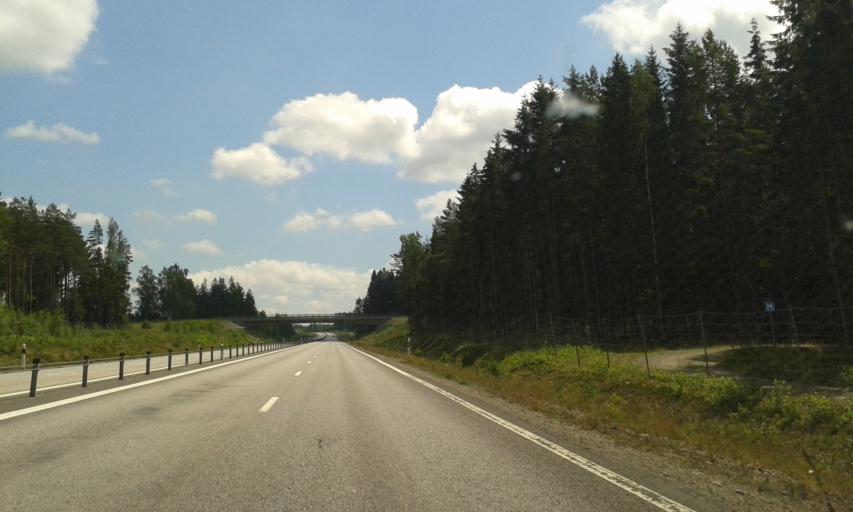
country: SE
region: Kronoberg
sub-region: Vaxjo Kommun
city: Gemla
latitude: 56.9147
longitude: 14.6250
